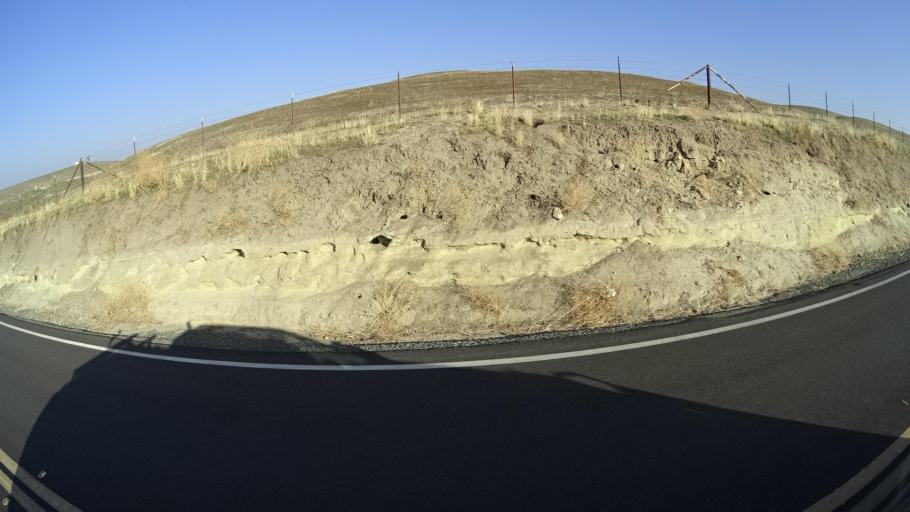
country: US
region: California
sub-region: Tulare County
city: Richgrove
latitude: 35.7460
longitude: -118.9277
